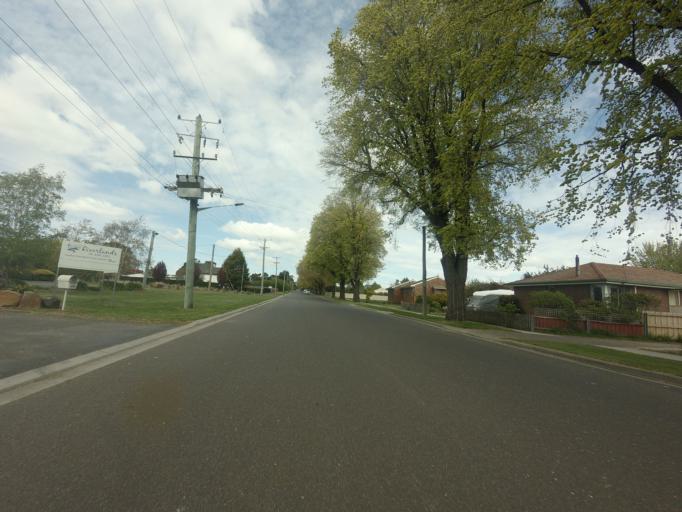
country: AU
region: Tasmania
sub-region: Northern Midlands
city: Longford
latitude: -41.6039
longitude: 147.1255
